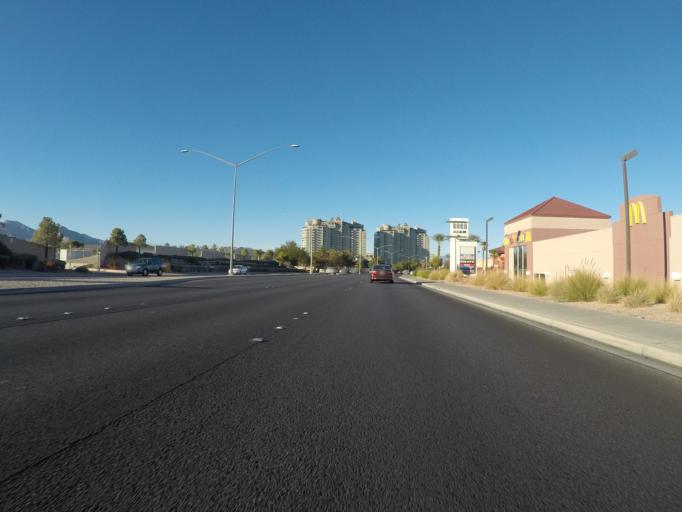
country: US
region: Nevada
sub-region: Clark County
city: Summerlin South
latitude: 36.1612
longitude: -115.2913
